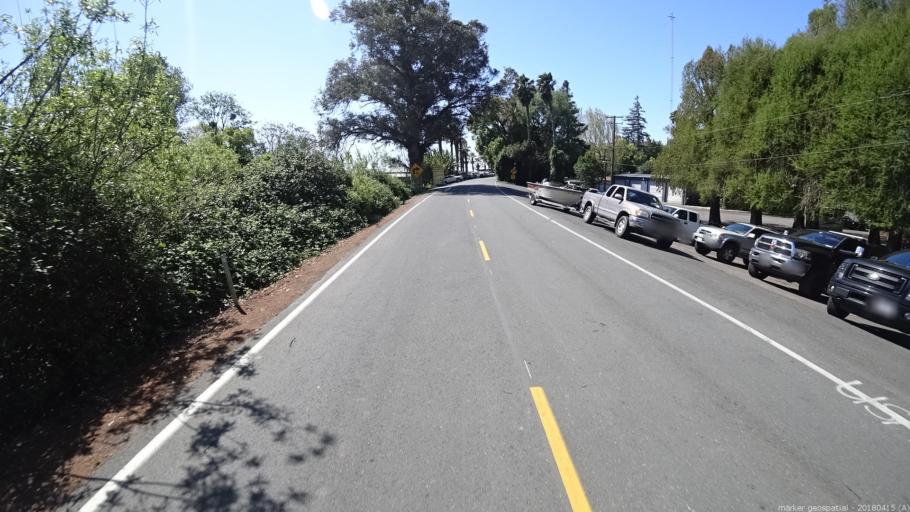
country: US
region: California
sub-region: Contra Costa County
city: Bethel Island
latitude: 38.0992
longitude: -121.5676
